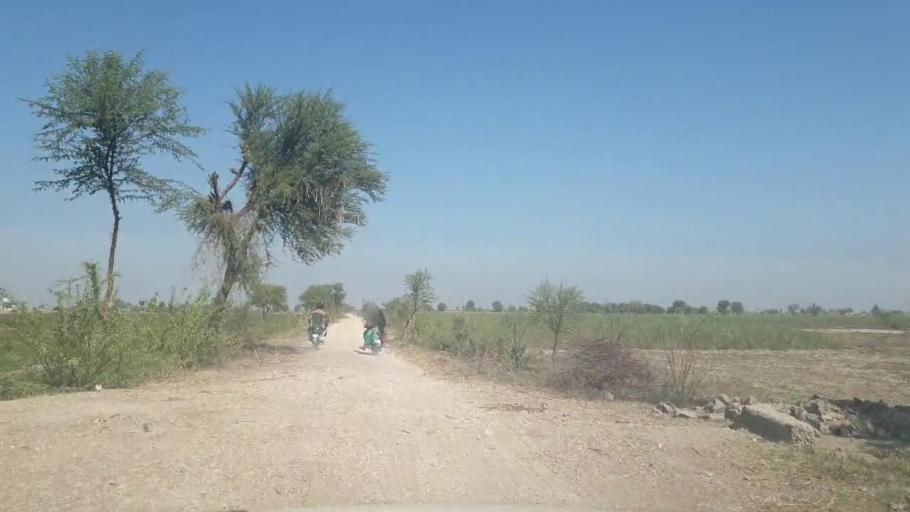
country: PK
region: Sindh
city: Mirpur Khas
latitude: 25.5538
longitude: 69.1966
